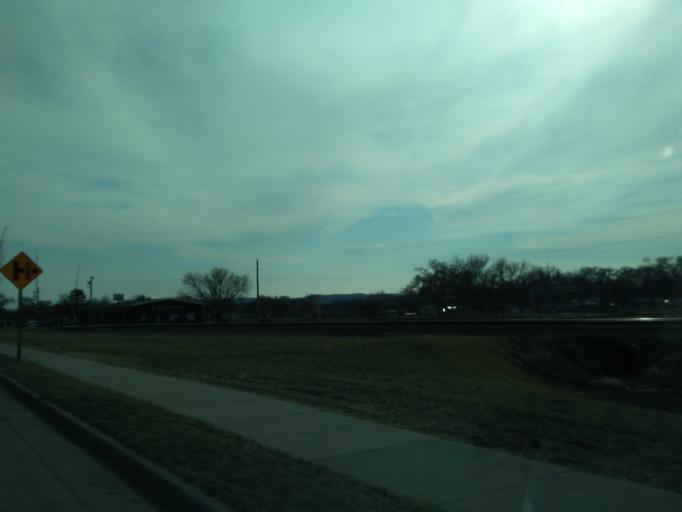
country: US
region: Wisconsin
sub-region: Crawford County
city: Prairie du Chien
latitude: 43.0440
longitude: -91.1409
